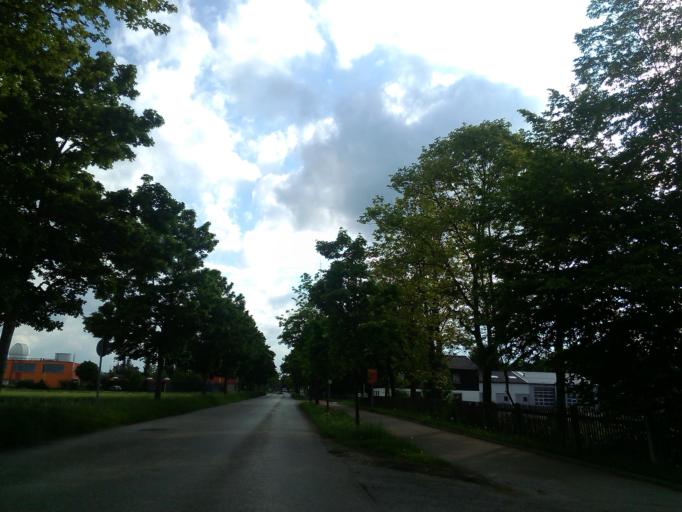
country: DE
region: Bavaria
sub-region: Upper Bavaria
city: Gilching
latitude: 48.1049
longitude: 11.3002
